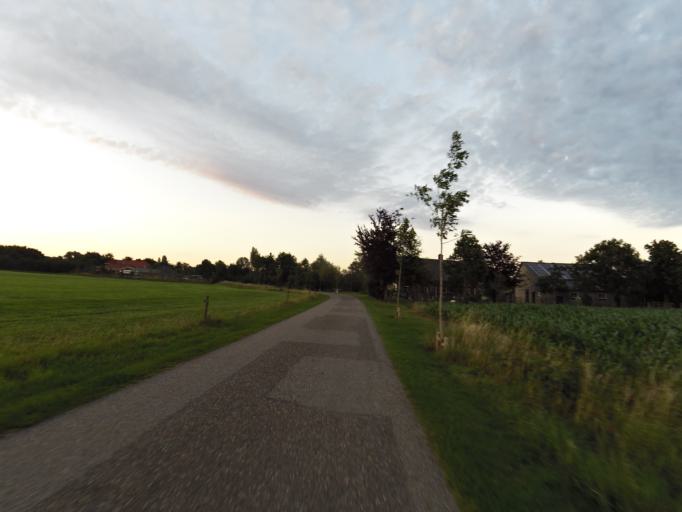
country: NL
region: Gelderland
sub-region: Oude IJsselstreek
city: Gendringen
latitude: 51.8355
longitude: 6.4012
